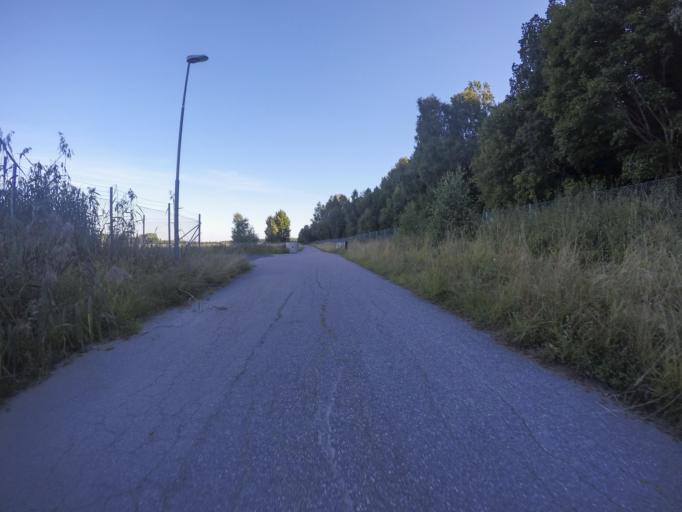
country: SE
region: Vaestmanland
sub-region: Vasteras
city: Vasteras
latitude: 59.5807
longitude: 16.6253
